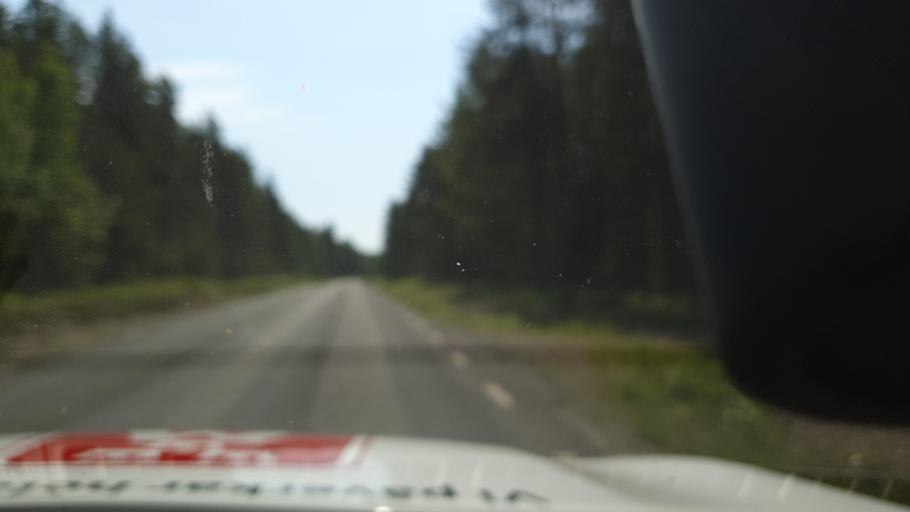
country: SE
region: Vaesterbotten
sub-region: Skelleftea Kommun
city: Langsele
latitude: 65.0230
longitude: 20.0716
